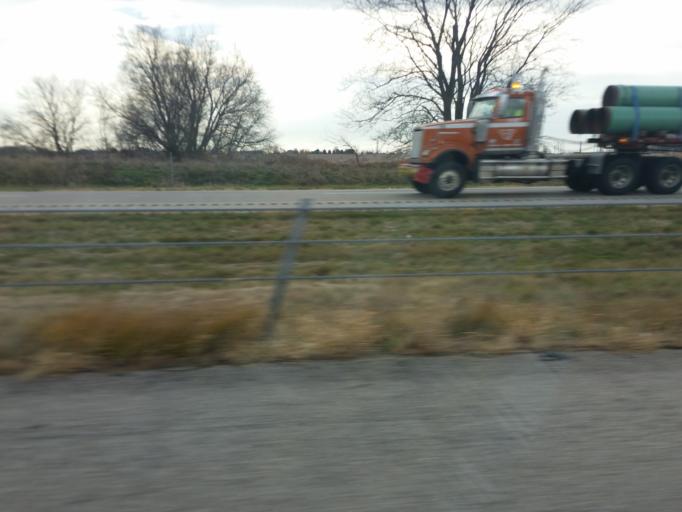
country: US
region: Iowa
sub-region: Scott County
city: Eldridge
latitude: 41.5954
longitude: -90.5481
